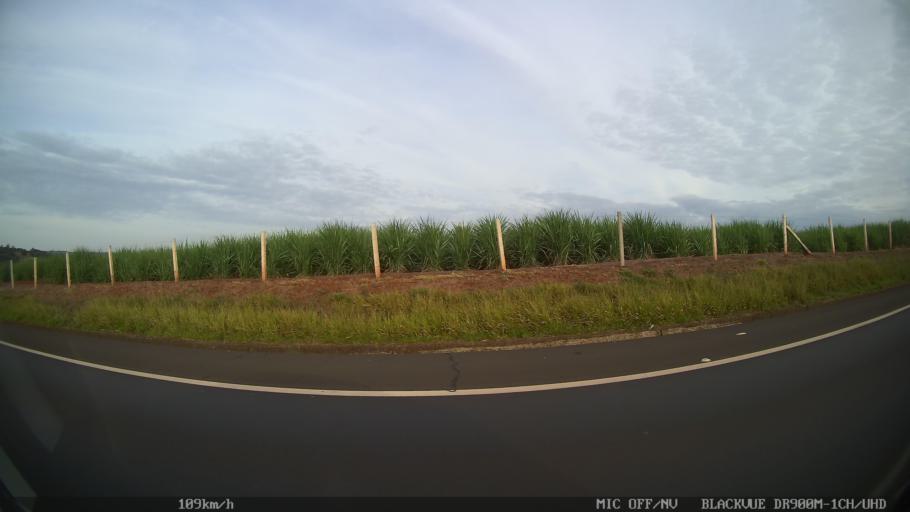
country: BR
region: Sao Paulo
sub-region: Iracemapolis
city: Iracemapolis
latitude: -22.6280
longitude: -47.5002
